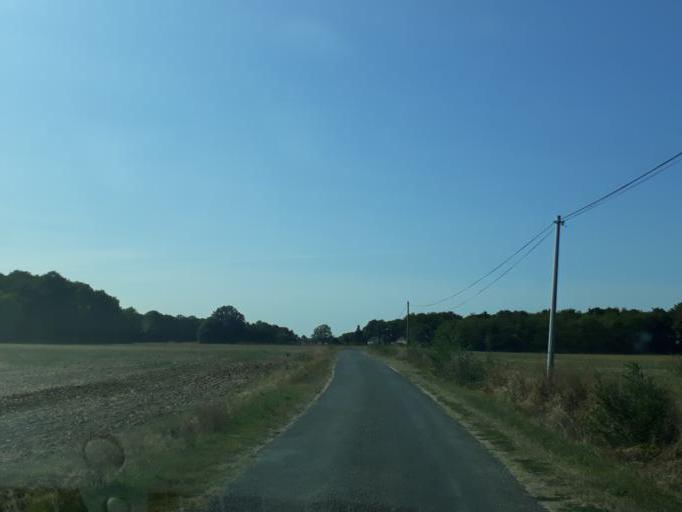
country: FR
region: Centre
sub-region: Departement de l'Indre
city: Chabris
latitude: 47.2625
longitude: 1.6326
